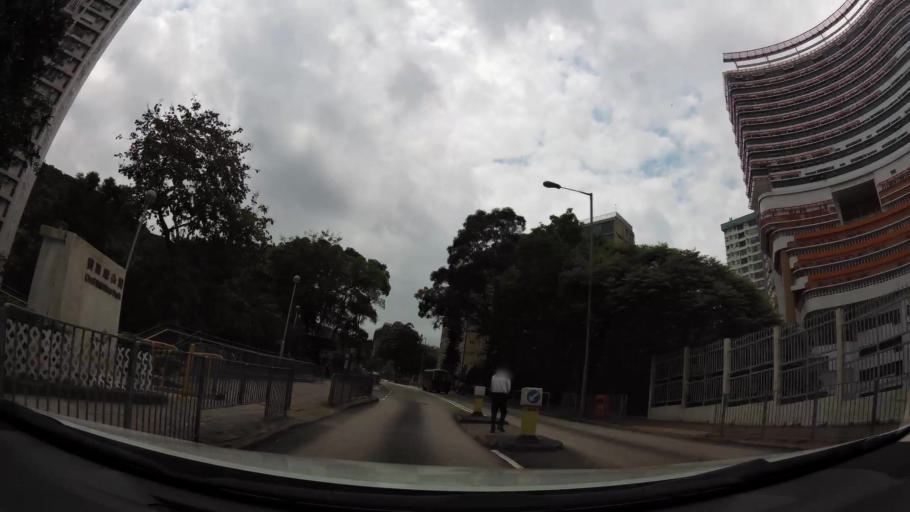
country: HK
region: Wanchai
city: Wan Chai
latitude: 22.2859
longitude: 114.1999
